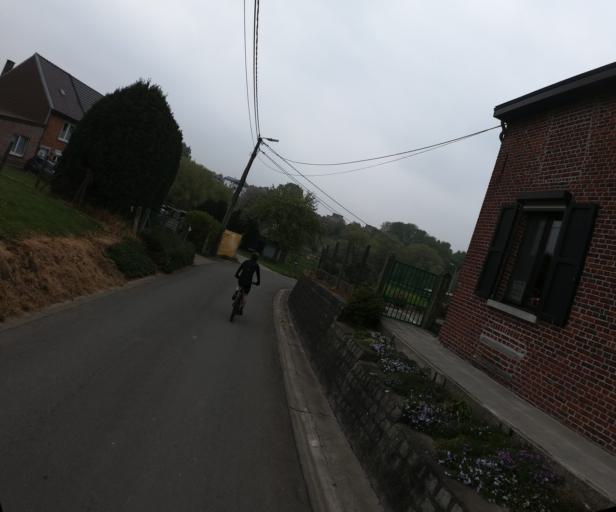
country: BE
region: Flanders
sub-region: Provincie Vlaams-Brabant
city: Pepingen
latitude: 50.7327
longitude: 4.1579
